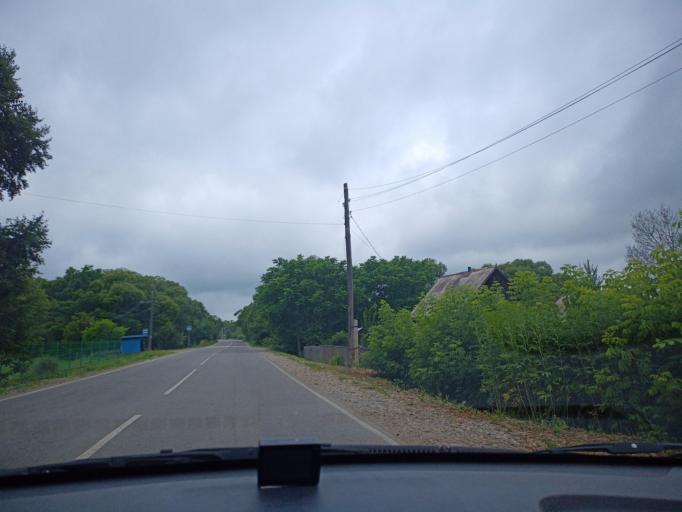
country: RU
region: Primorskiy
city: Novopokrovka
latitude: 45.8929
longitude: 134.8571
